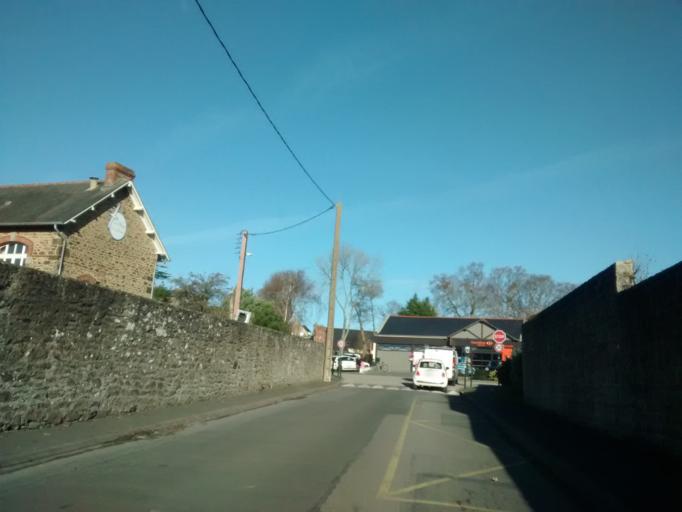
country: FR
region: Brittany
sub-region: Departement d'Ille-et-Vilaine
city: Saint-Briac-sur-Mer
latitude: 48.6180
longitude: -2.1285
